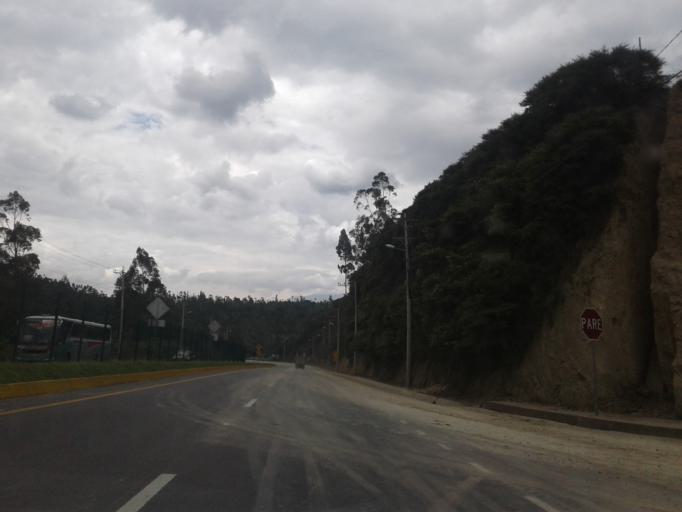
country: EC
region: Pichincha
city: Sangolqui
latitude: -0.3212
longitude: -78.3724
